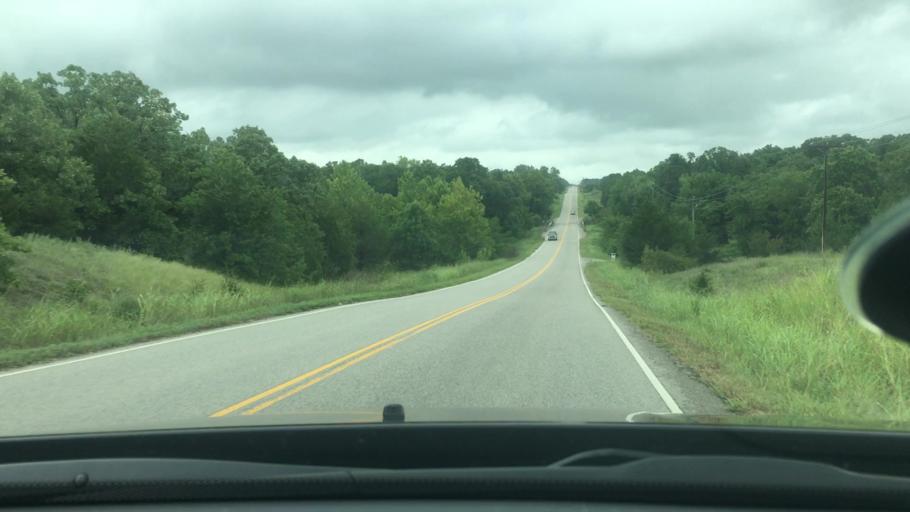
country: US
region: Oklahoma
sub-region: Bryan County
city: Calera
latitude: 33.9545
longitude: -96.5002
